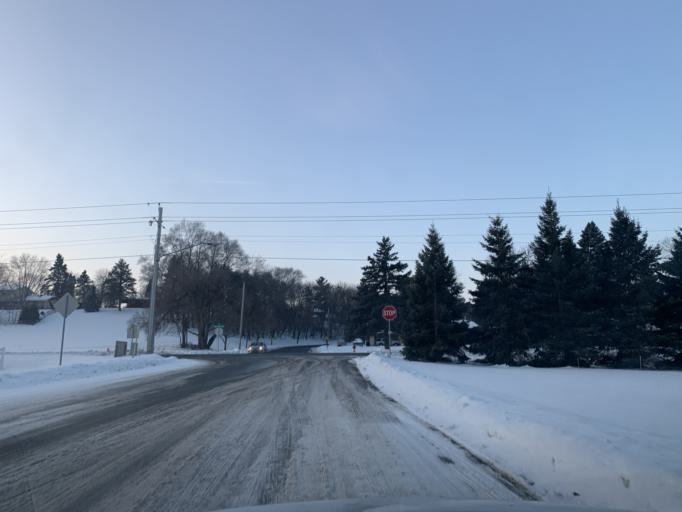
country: US
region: Minnesota
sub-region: Scott County
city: Shakopee
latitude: 44.7870
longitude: -93.4901
